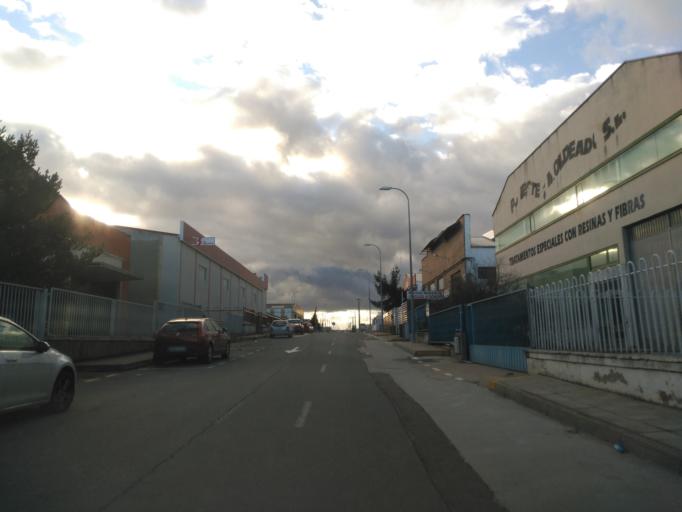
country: ES
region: Castille and Leon
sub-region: Provincia de Salamanca
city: Carbajosa de la Sagrada
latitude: 40.9446
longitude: -5.6575
